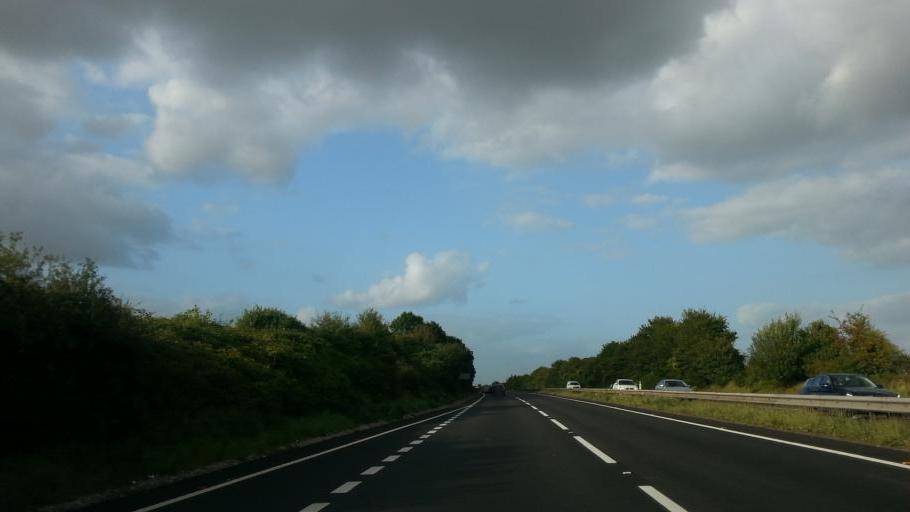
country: GB
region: England
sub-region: Hampshire
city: Kings Worthy
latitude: 51.1599
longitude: -1.3437
